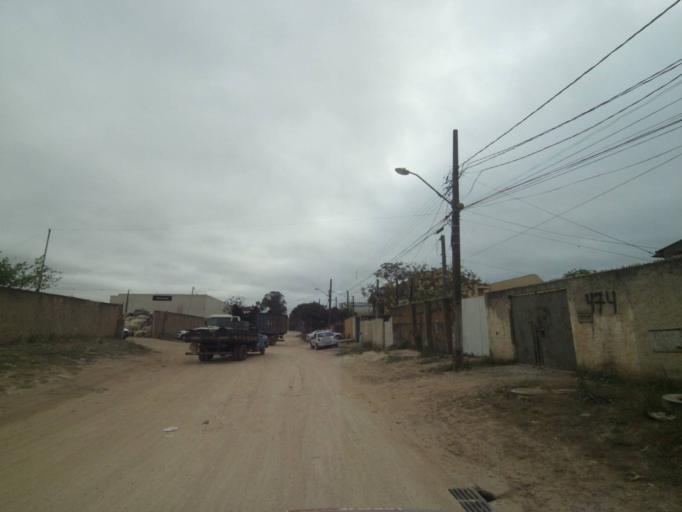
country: BR
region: Parana
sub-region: Sao Jose Dos Pinhais
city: Sao Jose dos Pinhais
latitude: -25.5045
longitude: -49.2140
